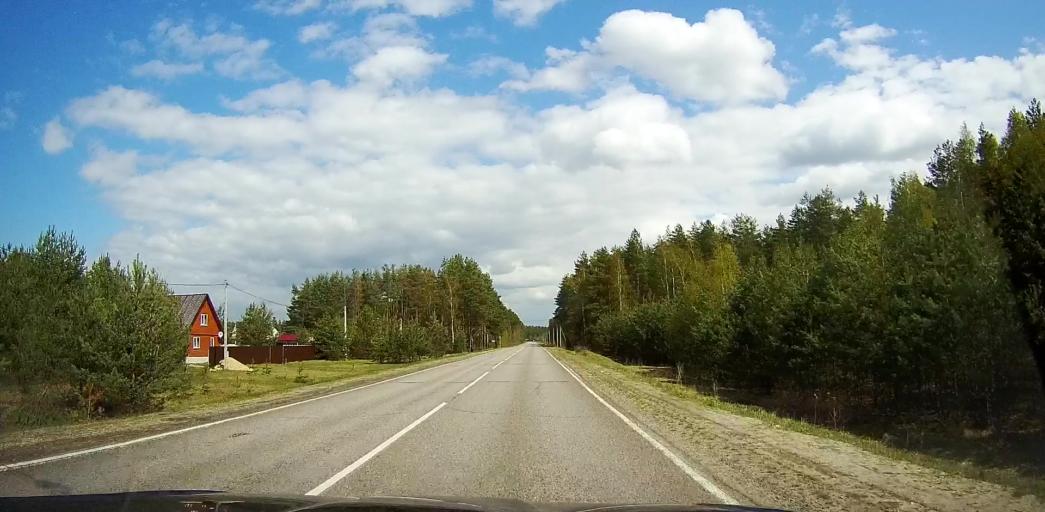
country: RU
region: Moskovskaya
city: Davydovo
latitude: 55.5534
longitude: 38.8212
